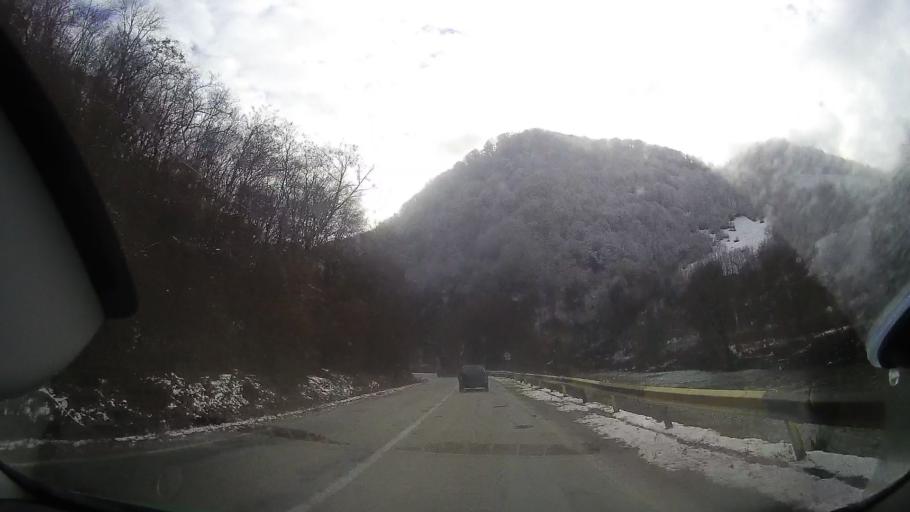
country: RO
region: Alba
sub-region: Oras Baia de Aries
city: Baia de Aries
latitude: 46.4061
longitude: 23.3364
